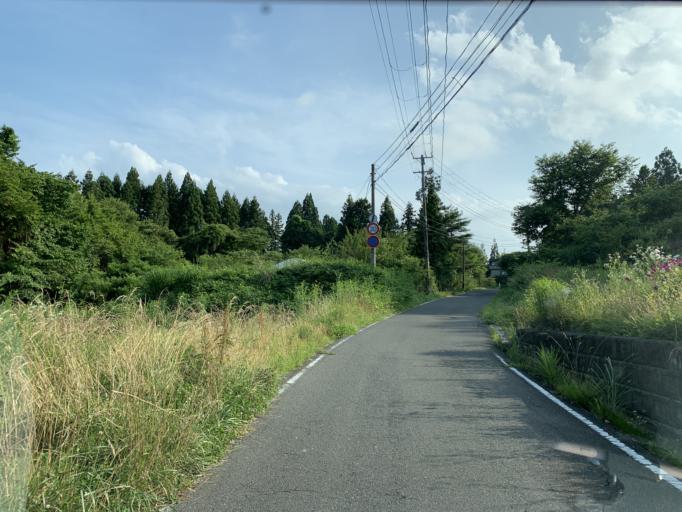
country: JP
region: Iwate
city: Ichinoseki
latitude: 38.8628
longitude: 141.1223
